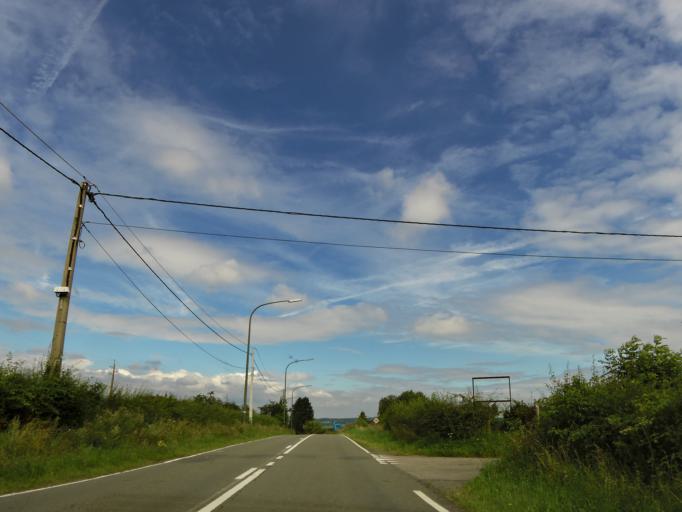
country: BE
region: Wallonia
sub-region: Province de Liege
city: Jalhay
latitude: 50.5123
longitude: 5.9514
